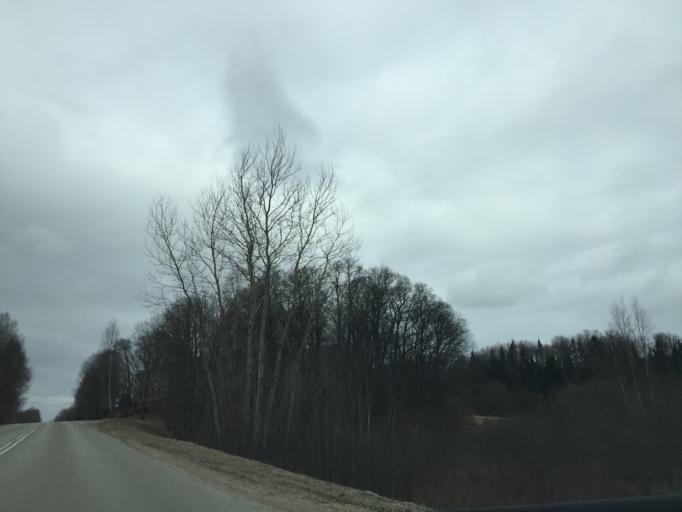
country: LV
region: Kraslavas Rajons
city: Kraslava
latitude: 55.9426
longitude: 27.1622
